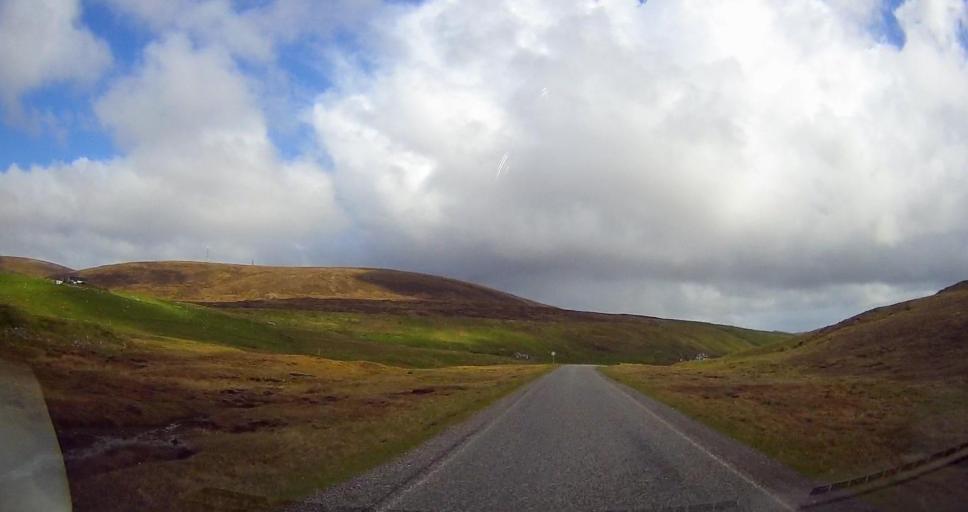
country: GB
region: Scotland
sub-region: Shetland Islands
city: Lerwick
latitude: 60.5200
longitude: -1.3774
